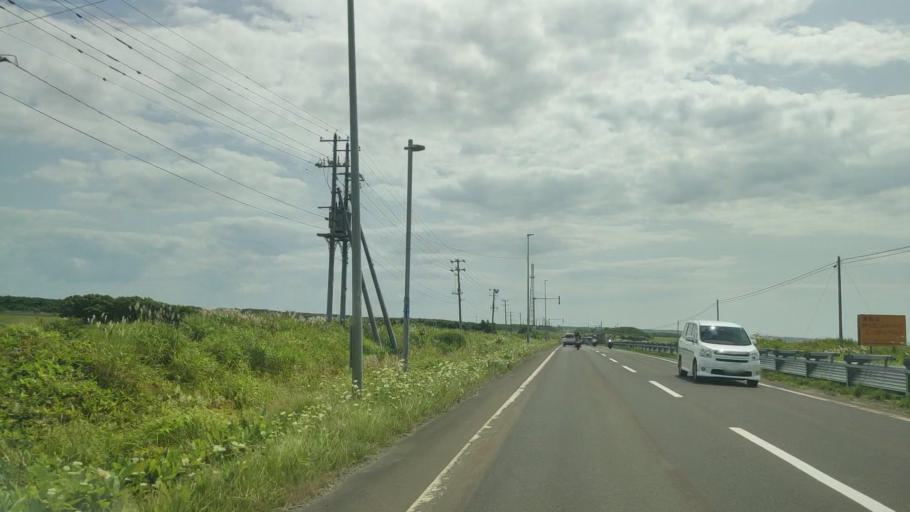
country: JP
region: Hokkaido
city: Rumoi
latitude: 44.4406
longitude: 141.7530
